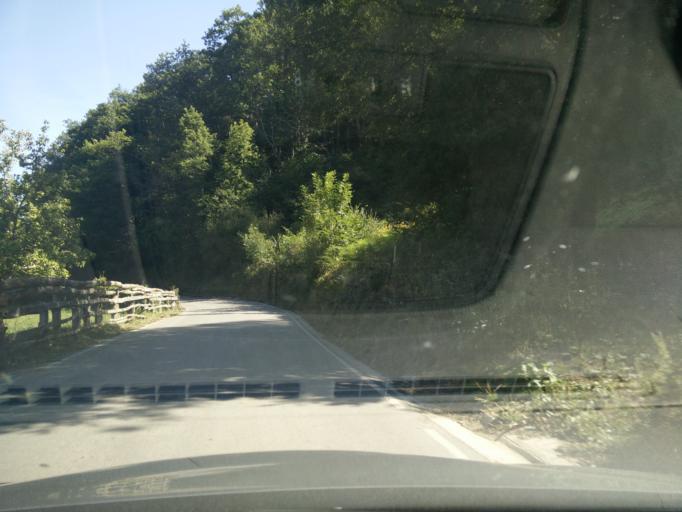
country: ES
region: Asturias
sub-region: Province of Asturias
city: Campo de Caso
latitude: 43.1573
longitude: -5.3923
